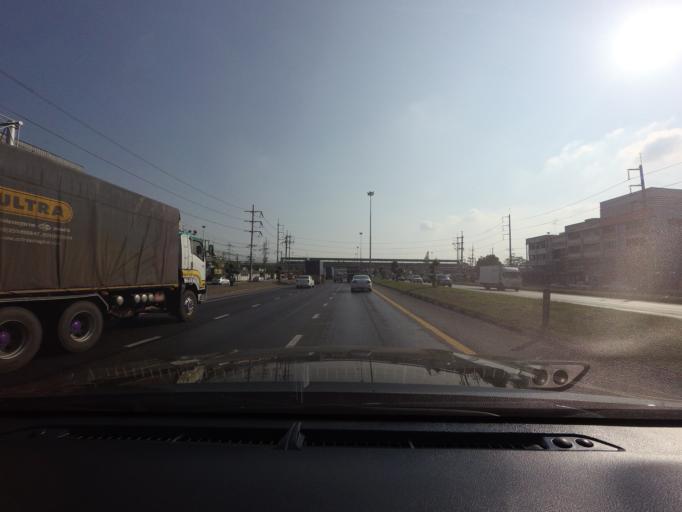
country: TH
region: Sara Buri
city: Nong Khae
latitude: 14.4063
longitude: 100.8907
